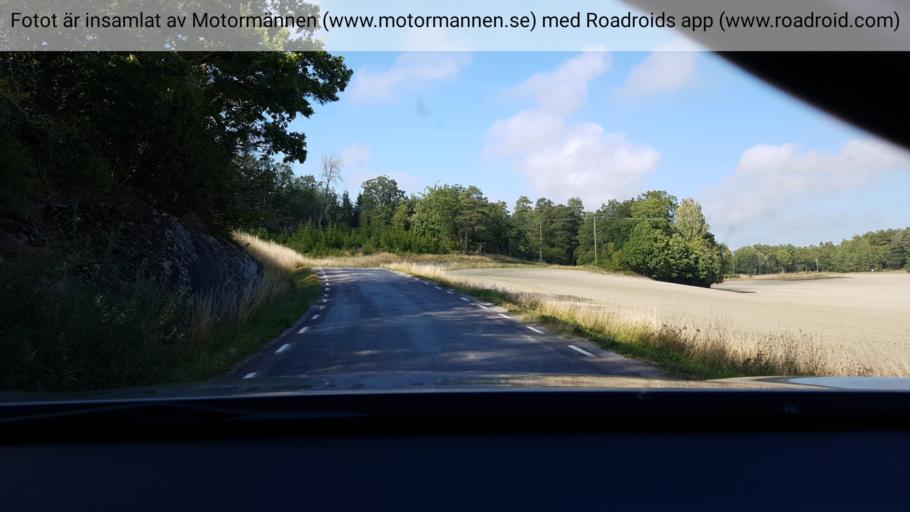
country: SE
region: Stockholm
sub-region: Nynashamns Kommun
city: Osmo
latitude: 58.8930
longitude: 17.7938
